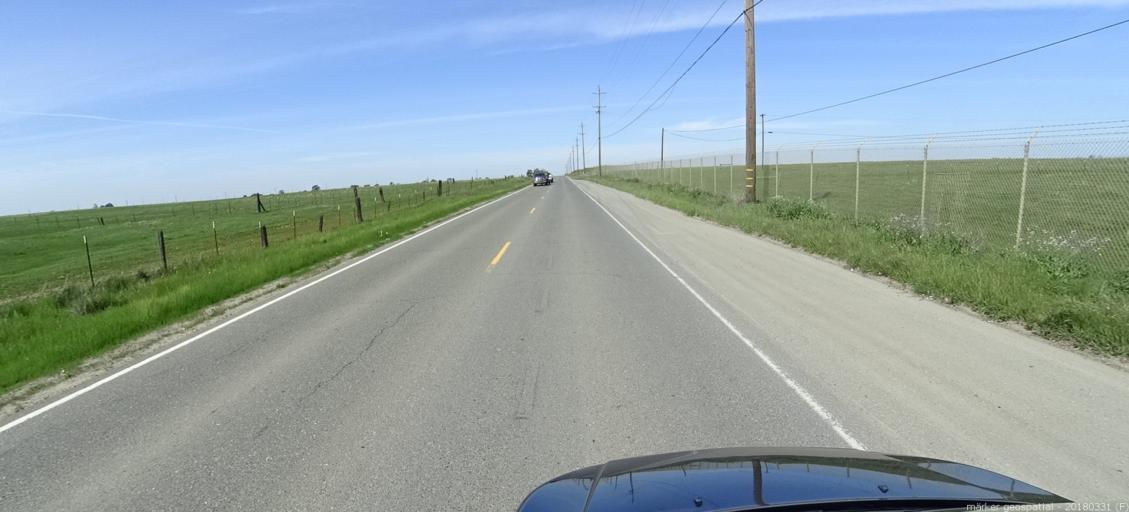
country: US
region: California
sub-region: Sacramento County
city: Rancho Murieta
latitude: 38.5155
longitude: -121.1964
